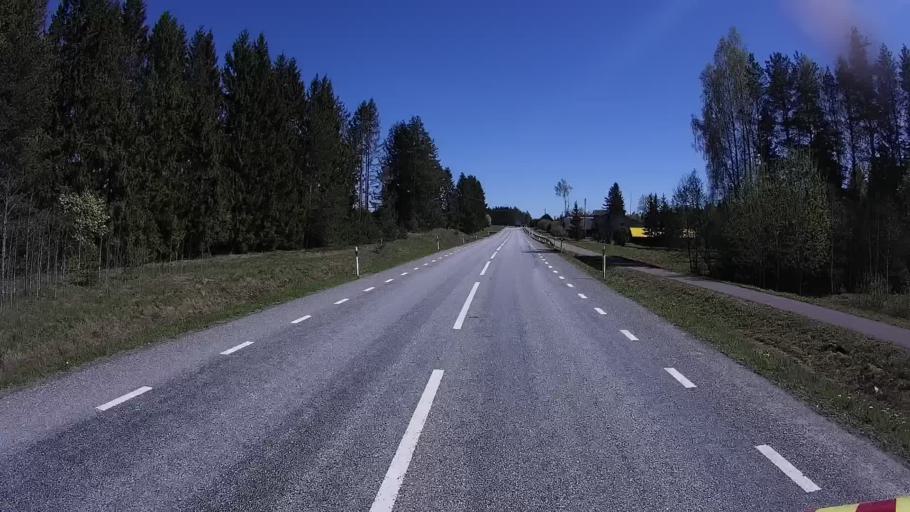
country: EE
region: Laeaene-Virumaa
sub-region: Tapa vald
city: Tapa
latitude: 59.2568
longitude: 25.6664
